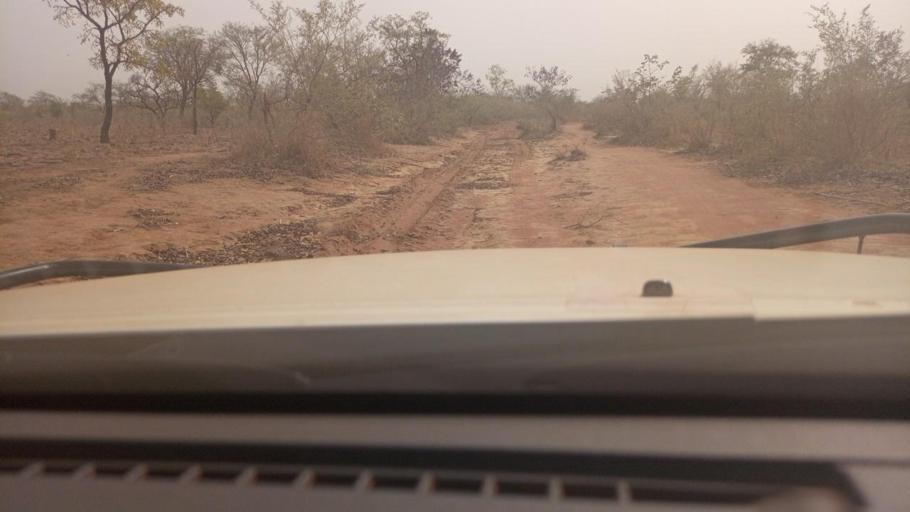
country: BF
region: Boucle du Mouhoun
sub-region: Province des Banwa
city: Salanso
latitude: 12.1623
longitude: -4.2400
